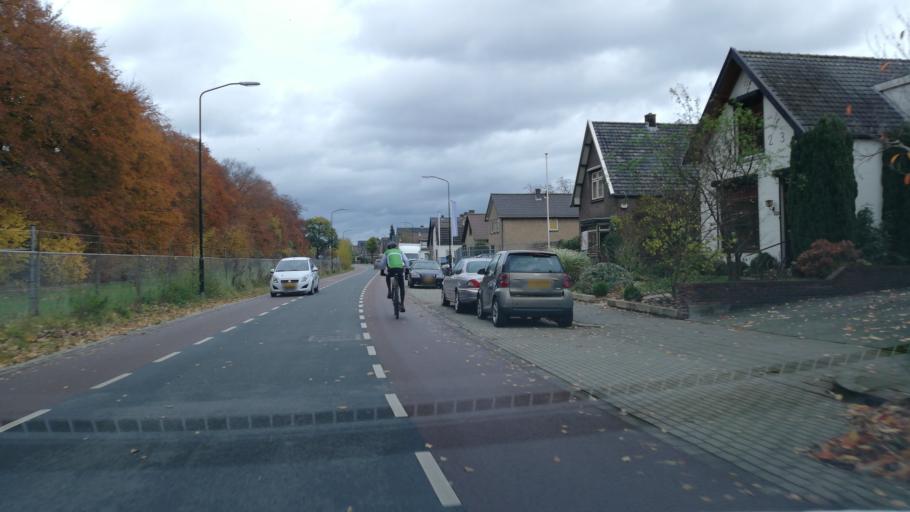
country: NL
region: Gelderland
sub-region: Gemeente Apeldoorn
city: Apeldoorn
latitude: 52.1913
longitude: 5.9449
